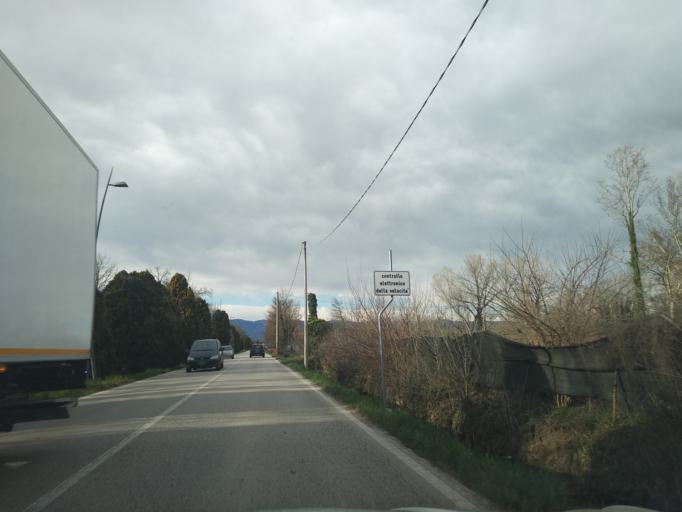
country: IT
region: Veneto
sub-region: Provincia di Vicenza
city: Bolzano Vicentino
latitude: 45.5938
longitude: 11.6230
